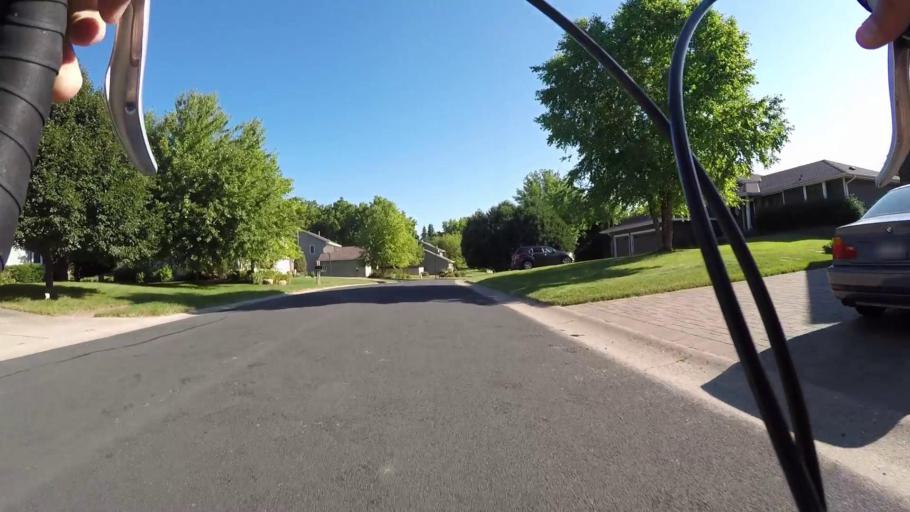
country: US
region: Minnesota
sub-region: Carver County
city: Chanhassen
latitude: 44.8702
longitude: -93.5084
